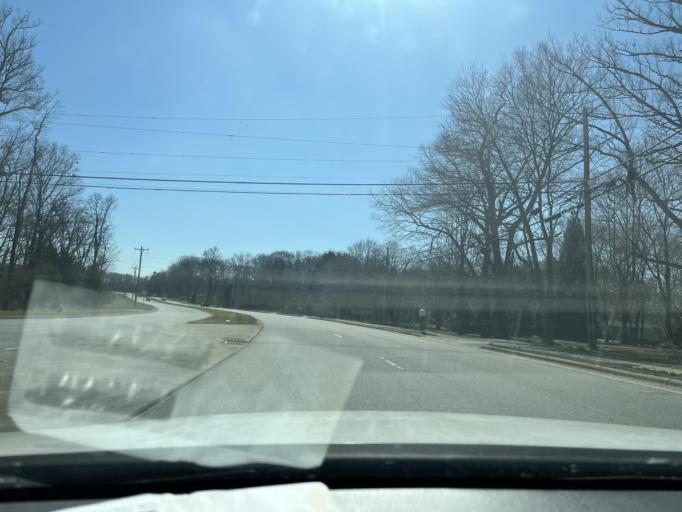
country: US
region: North Carolina
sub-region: Guilford County
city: Jamestown
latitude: 36.0209
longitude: -79.9266
